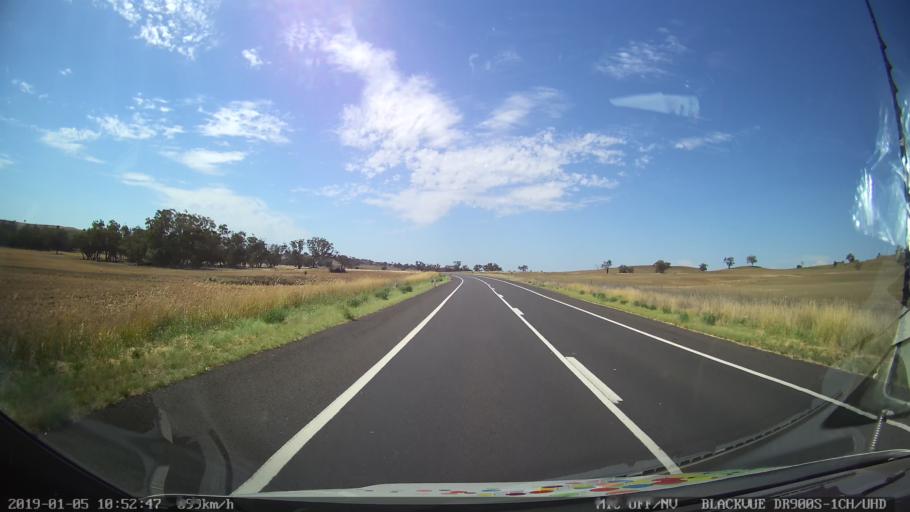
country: AU
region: New South Wales
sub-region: Warrumbungle Shire
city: Coonabarabran
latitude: -31.4363
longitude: 149.1058
